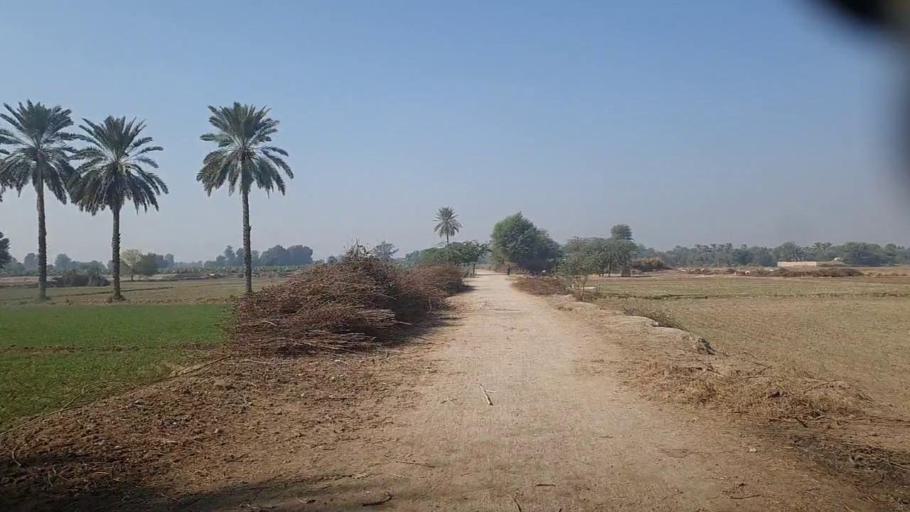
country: PK
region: Sindh
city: Kandiari
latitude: 27.0203
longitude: 68.5059
